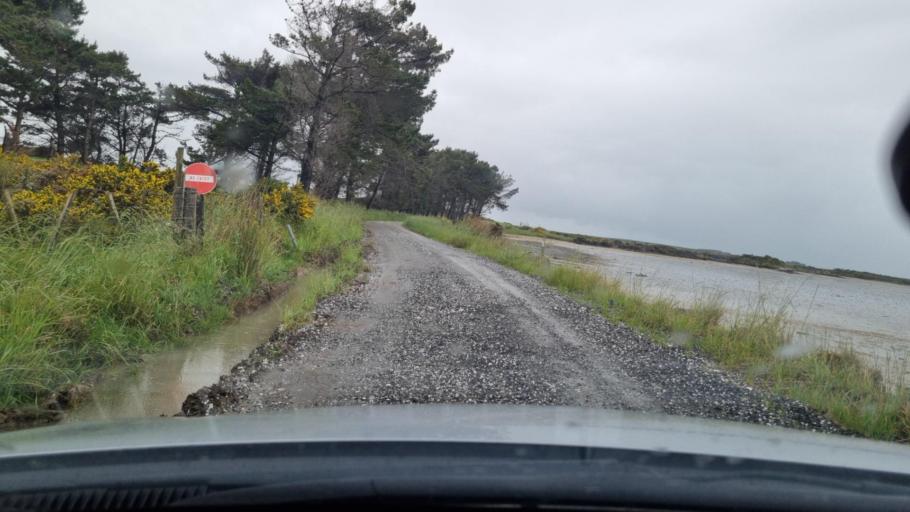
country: NZ
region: Southland
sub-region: Invercargill City
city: Bluff
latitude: -46.5484
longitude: 168.3113
